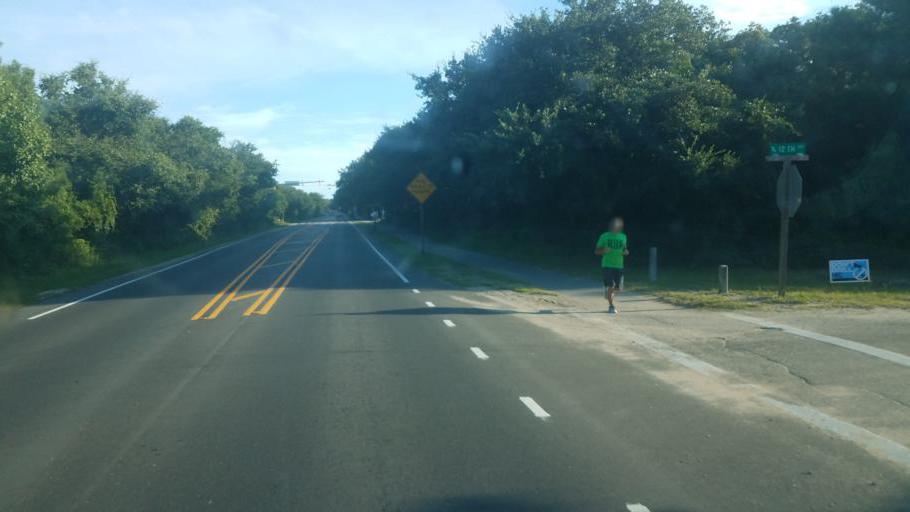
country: US
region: North Carolina
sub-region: Dare County
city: Southern Shores
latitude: 36.1490
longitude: -75.7416
